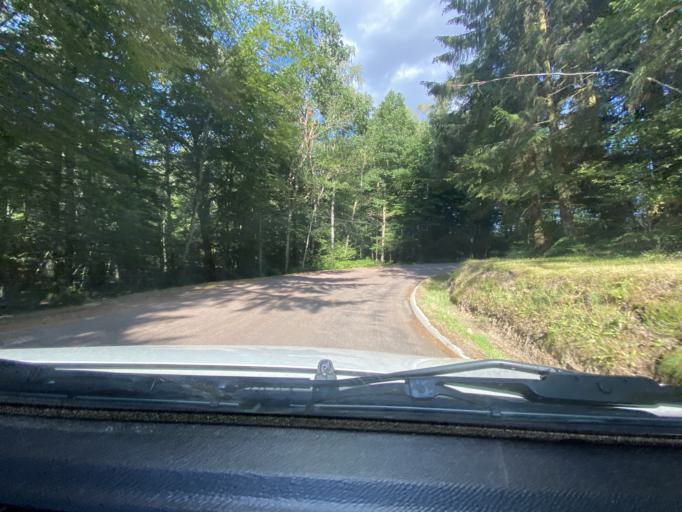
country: FR
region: Bourgogne
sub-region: Departement de la Cote-d'Or
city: Saulieu
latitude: 47.3113
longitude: 4.1950
